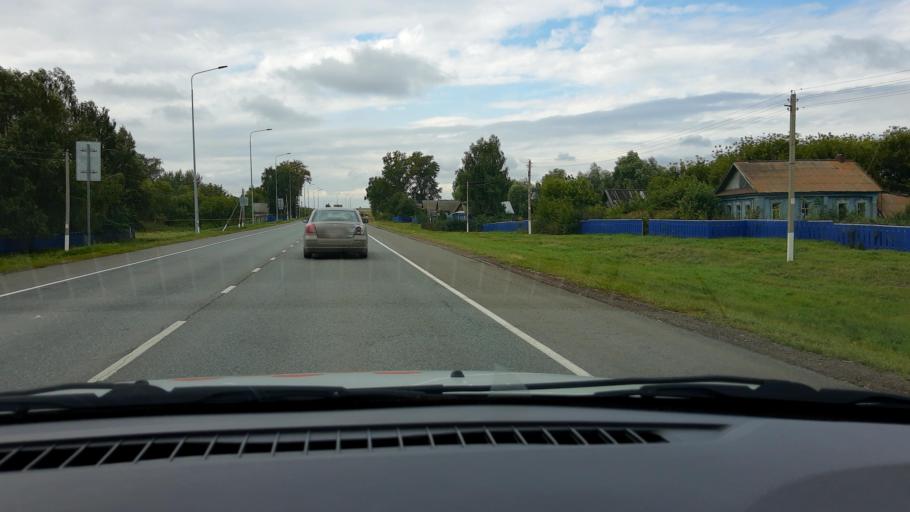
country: RU
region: Tatarstan
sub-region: Alekseyevskiy Rayon
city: Alekseyevskoye
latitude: 55.3103
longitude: 50.3010
